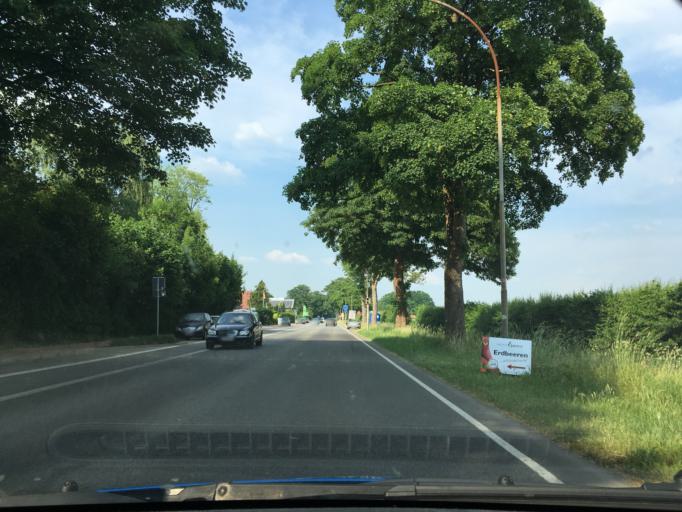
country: DE
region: Lower Saxony
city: Buchholz in der Nordheide
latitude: 53.3816
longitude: 9.8988
